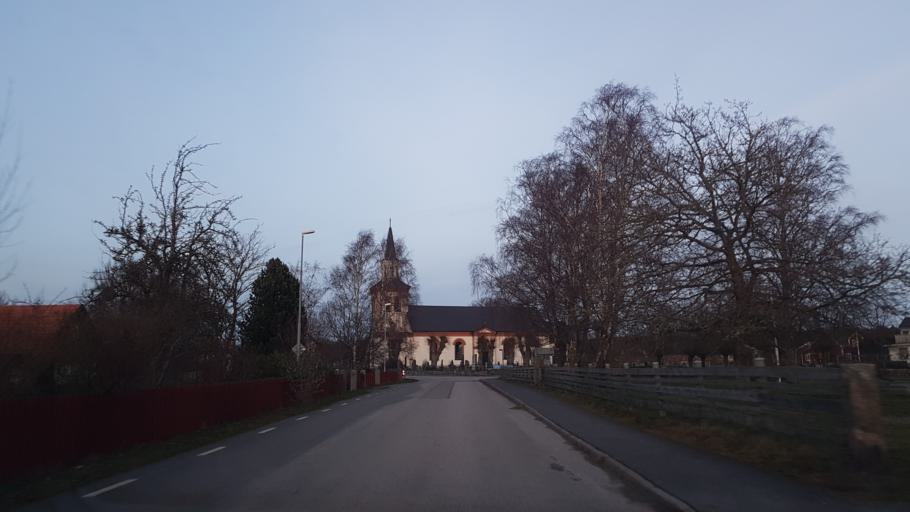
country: SE
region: Blekinge
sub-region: Karlskrona Kommun
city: Jaemjoe
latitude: 56.0940
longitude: 15.8318
